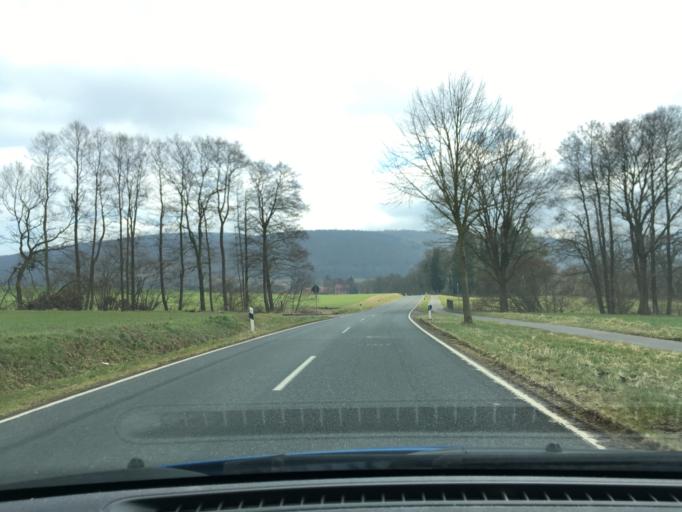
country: DE
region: Lower Saxony
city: Buhren
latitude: 51.5476
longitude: 9.6190
